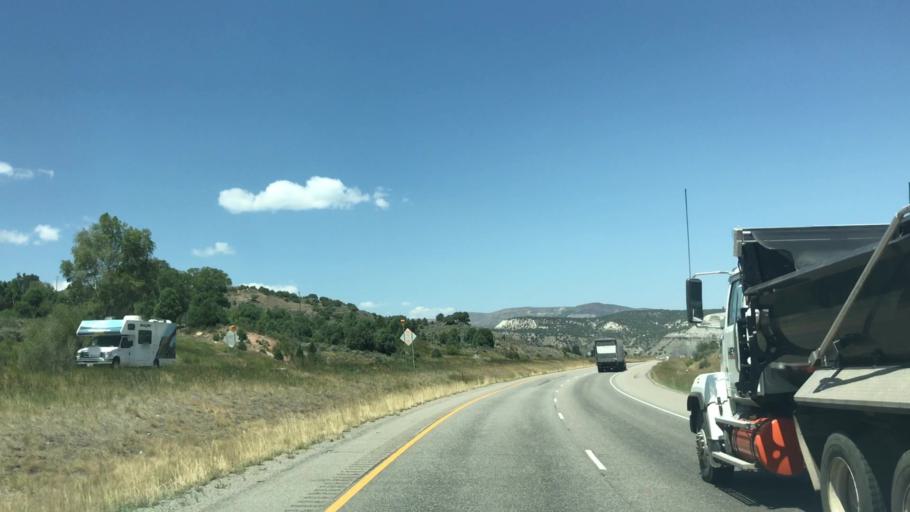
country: US
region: Colorado
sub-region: Eagle County
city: Edwards
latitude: 39.6848
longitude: -106.6603
